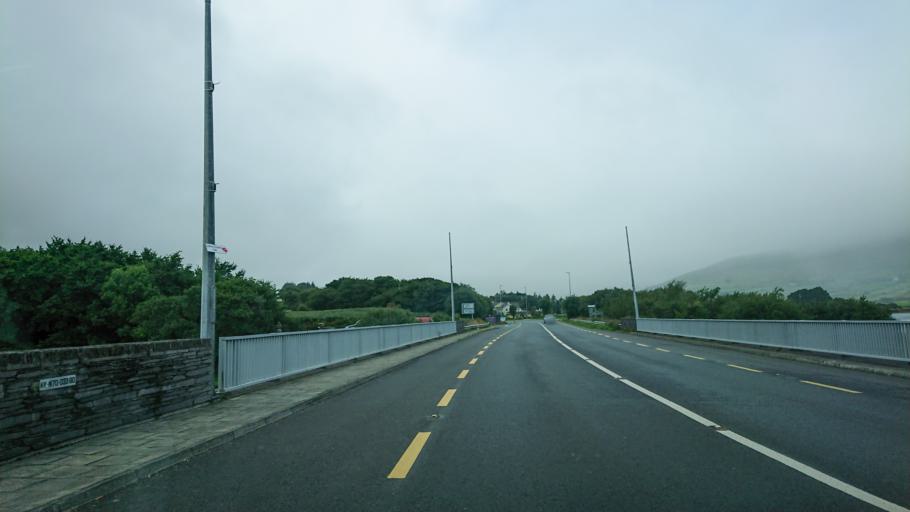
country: IE
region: Munster
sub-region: Ciarrai
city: Cahersiveen
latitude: 51.9516
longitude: -10.2035
